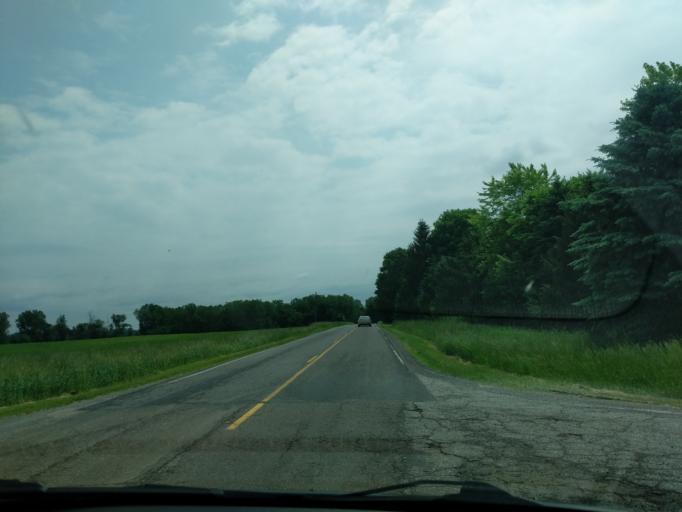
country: US
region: Michigan
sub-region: Ingham County
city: Williamston
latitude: 42.6933
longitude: -84.2302
